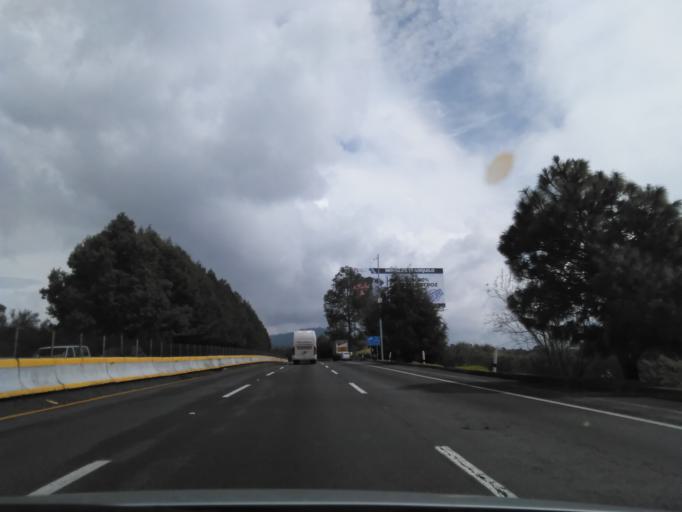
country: MX
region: Morelos
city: Tres Marias
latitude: 19.0845
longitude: -99.2231
